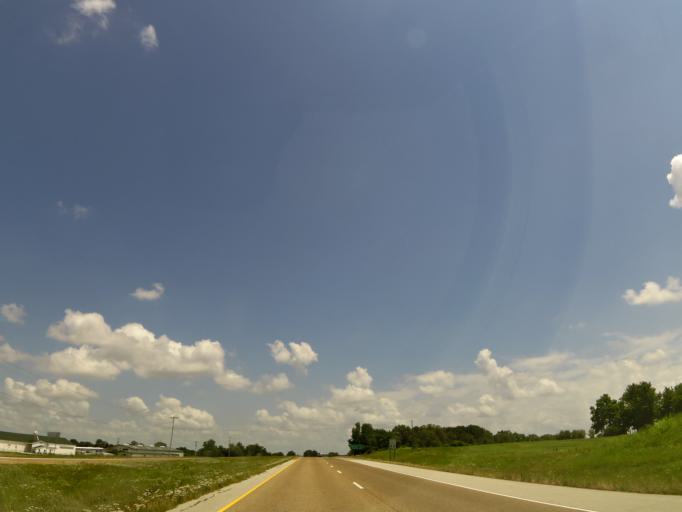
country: US
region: Tennessee
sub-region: Crockett County
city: Alamo
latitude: 35.8180
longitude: -89.1662
